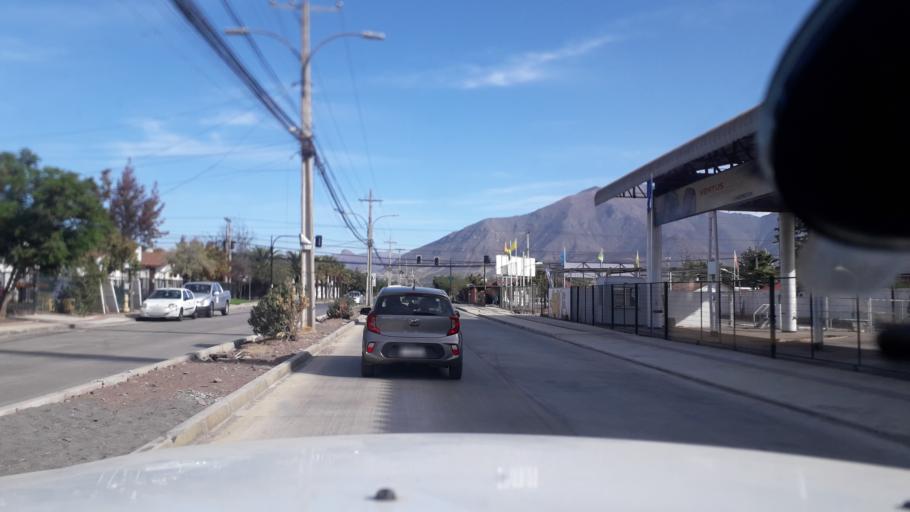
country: CL
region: Valparaiso
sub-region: Provincia de San Felipe
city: San Felipe
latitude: -32.7527
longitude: -70.7117
